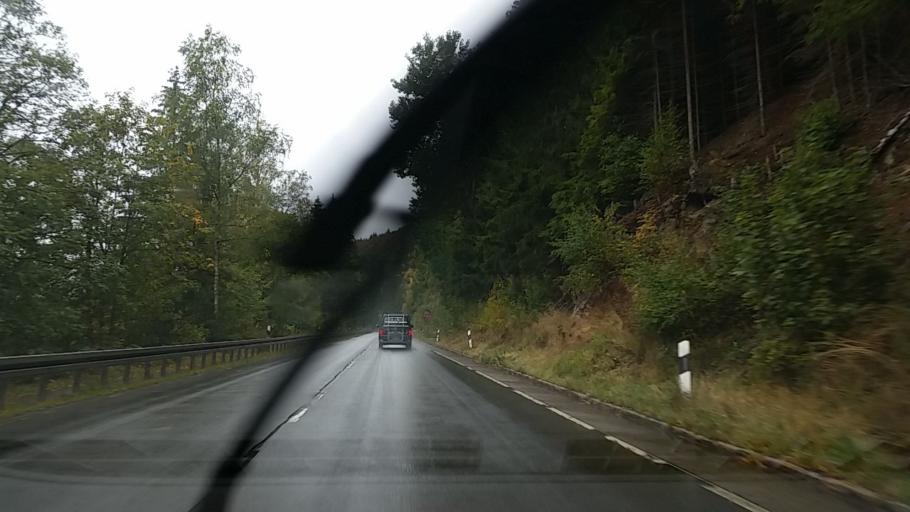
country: DE
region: Lower Saxony
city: Schulenberg im Oberharz
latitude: 51.8499
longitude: 10.4543
